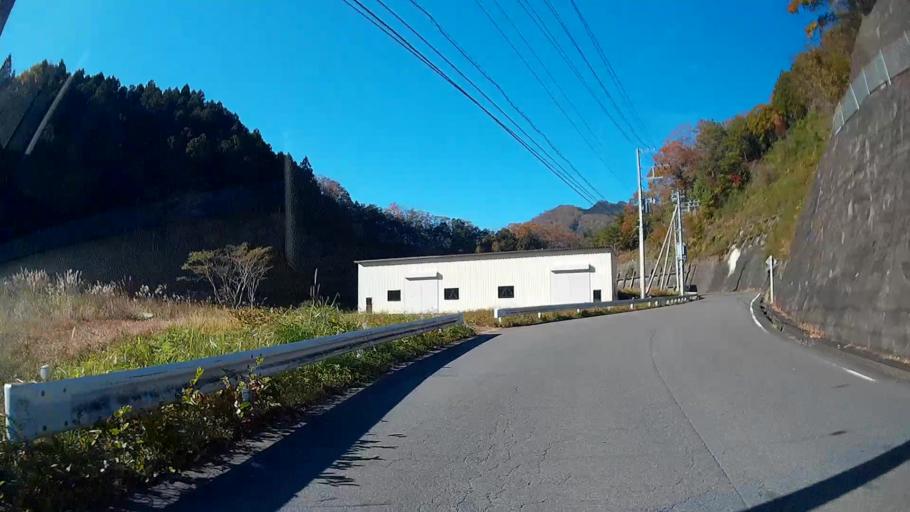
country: JP
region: Yamanashi
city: Uenohara
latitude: 35.5781
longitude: 139.1026
